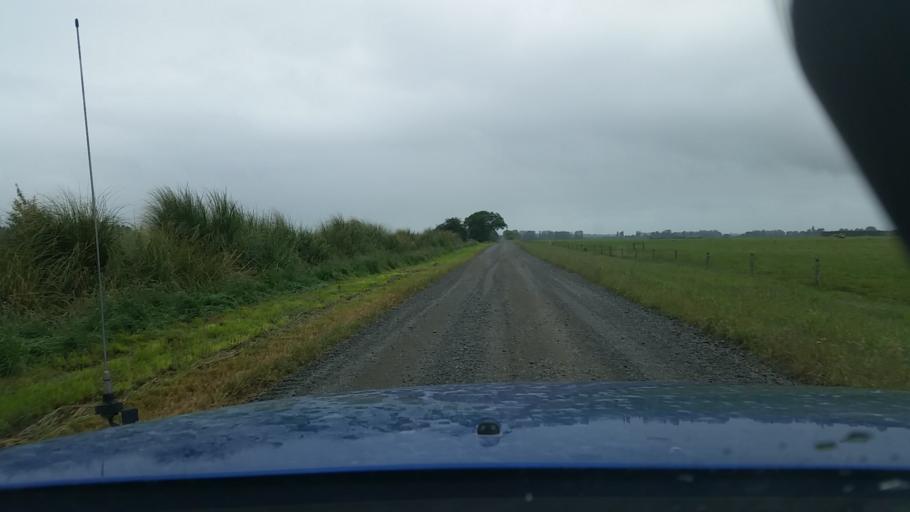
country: NZ
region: Canterbury
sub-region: Ashburton District
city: Tinwald
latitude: -43.9999
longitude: 171.6492
